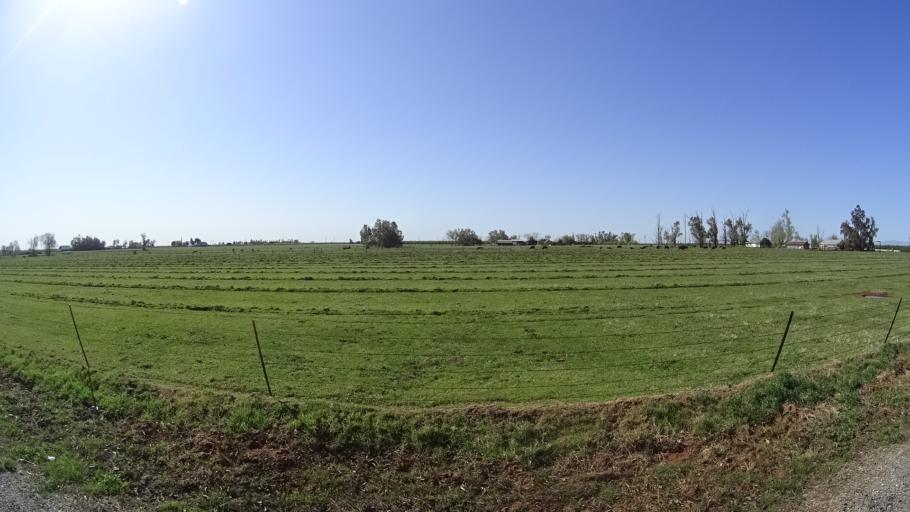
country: US
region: California
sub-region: Glenn County
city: Hamilton City
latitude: 39.7827
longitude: -122.0630
